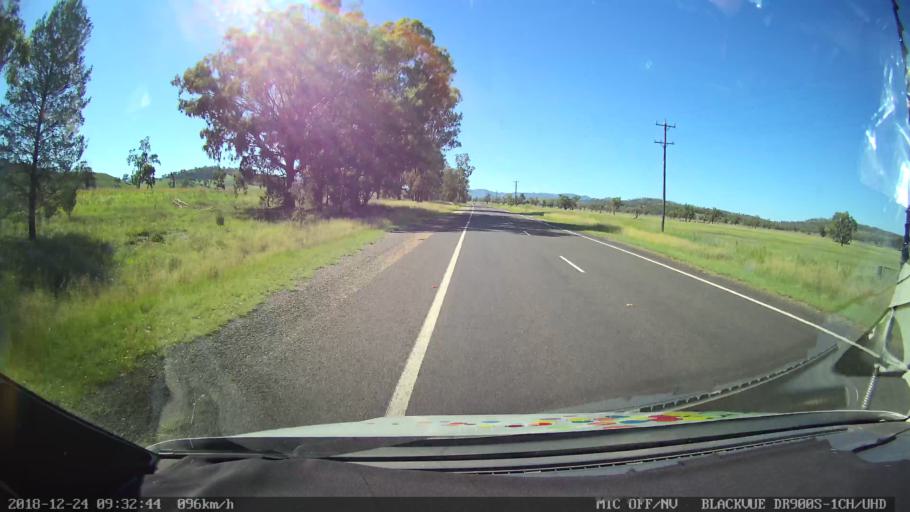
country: AU
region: New South Wales
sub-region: Liverpool Plains
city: Quirindi
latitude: -31.5944
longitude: 150.7038
